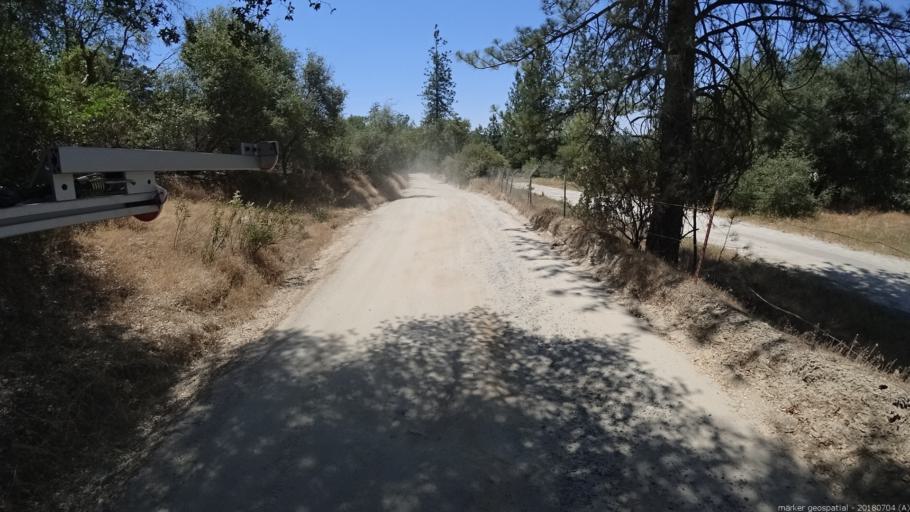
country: US
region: California
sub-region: Fresno County
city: Auberry
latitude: 37.2356
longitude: -119.4904
